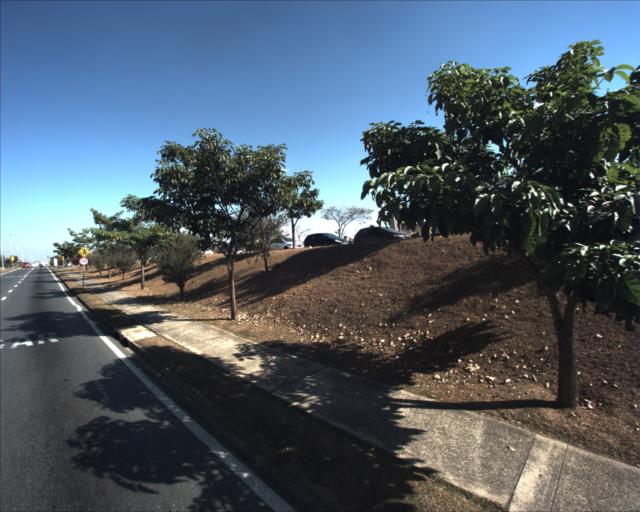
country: BR
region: Sao Paulo
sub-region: Sorocaba
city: Sorocaba
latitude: -23.4766
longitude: -47.4221
